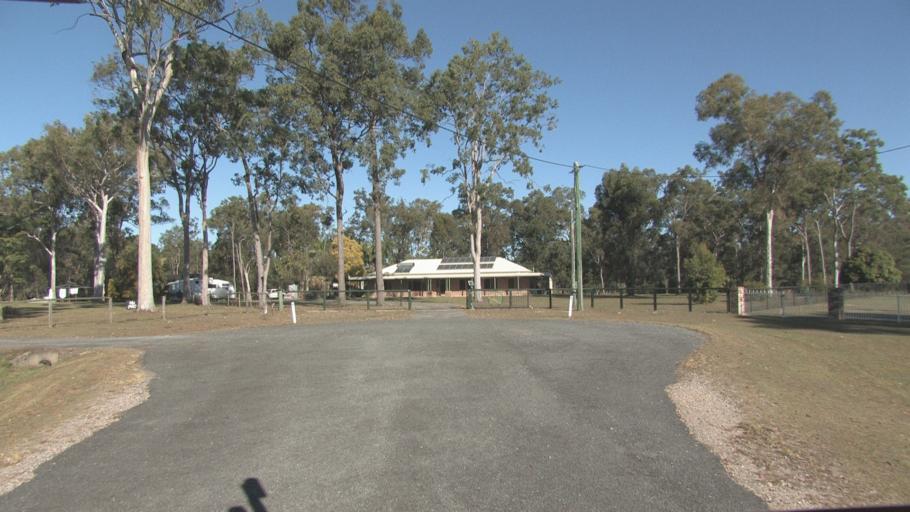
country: AU
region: Queensland
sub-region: Logan
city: Chambers Flat
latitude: -27.7385
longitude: 153.0749
